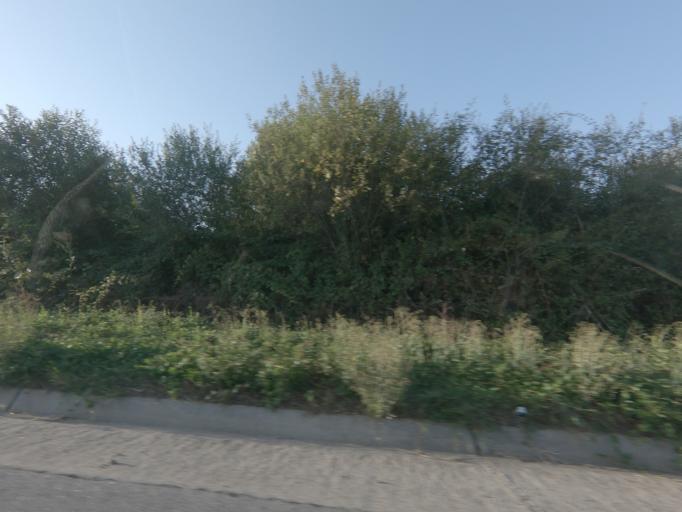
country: PT
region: Vila Real
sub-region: Sabrosa
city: Sabrosa
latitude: 41.2624
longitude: -7.6132
